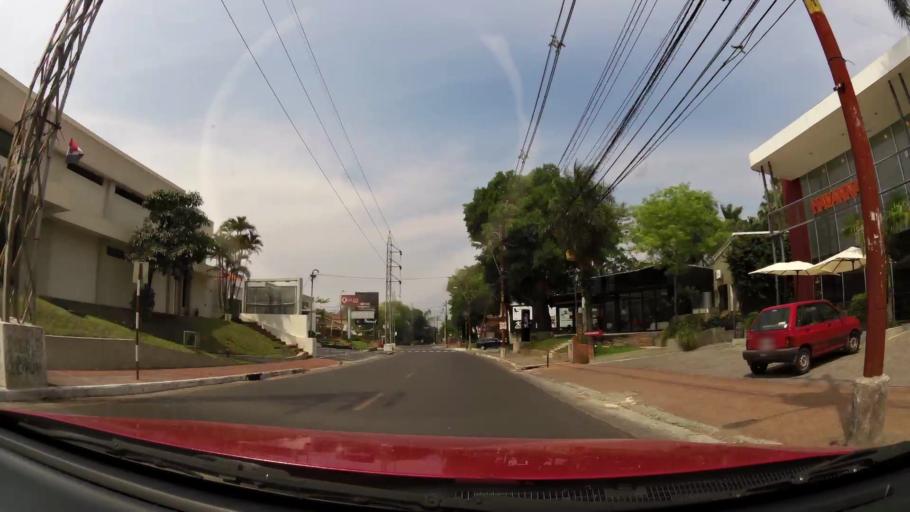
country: PY
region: Asuncion
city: Asuncion
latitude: -25.2878
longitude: -57.5998
